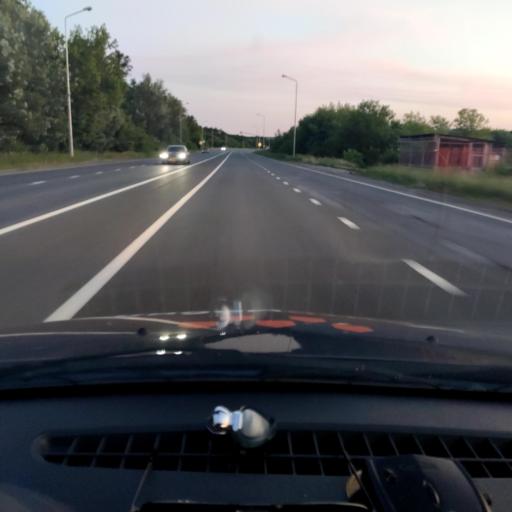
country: RU
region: Belgorod
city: Staryy Oskol
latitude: 51.3505
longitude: 37.8276
